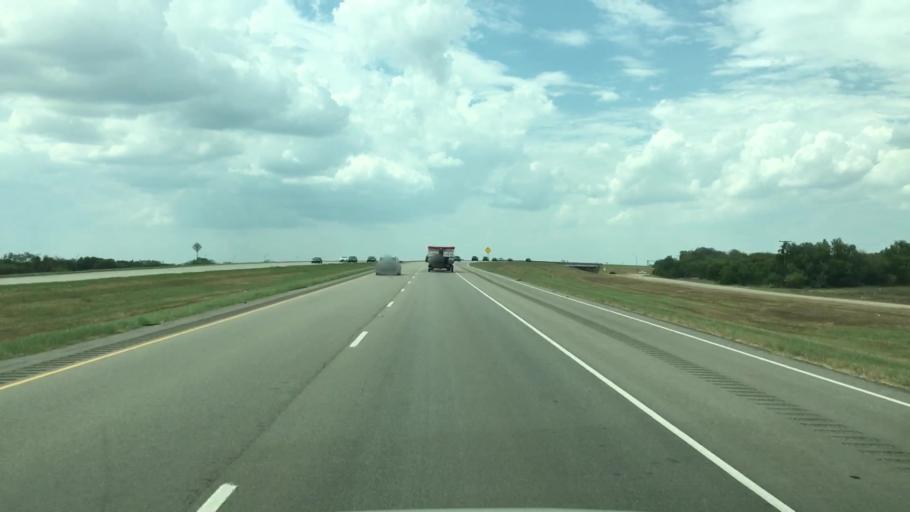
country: US
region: Texas
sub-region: Live Oak County
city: Three Rivers
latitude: 28.5221
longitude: -98.1825
